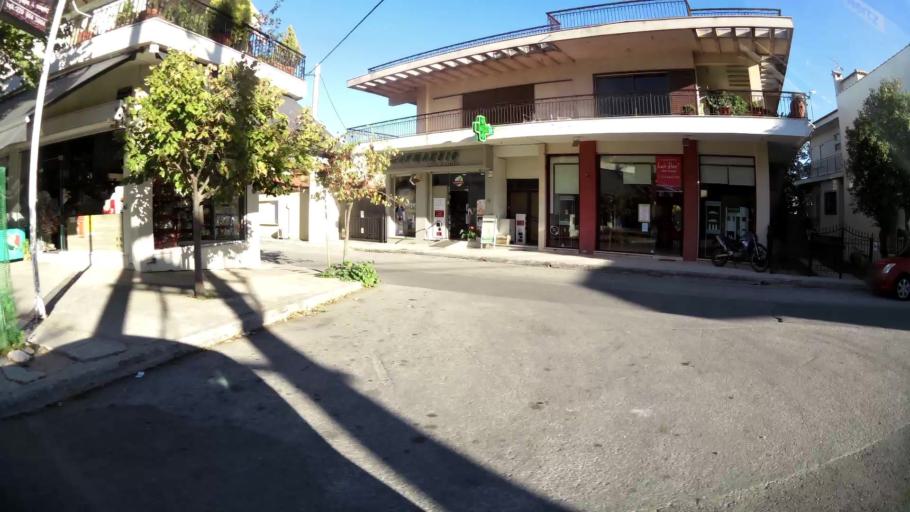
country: GR
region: Attica
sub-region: Nomarchia Anatolikis Attikis
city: Paiania
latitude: 37.9579
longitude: 23.8523
